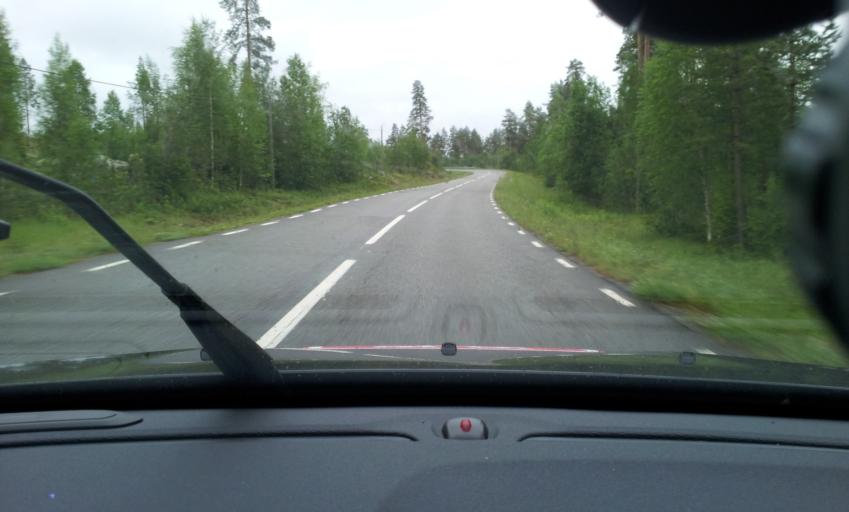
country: SE
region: Jaemtland
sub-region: Stroemsunds Kommun
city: Stroemsund
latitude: 63.3768
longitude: 15.6921
